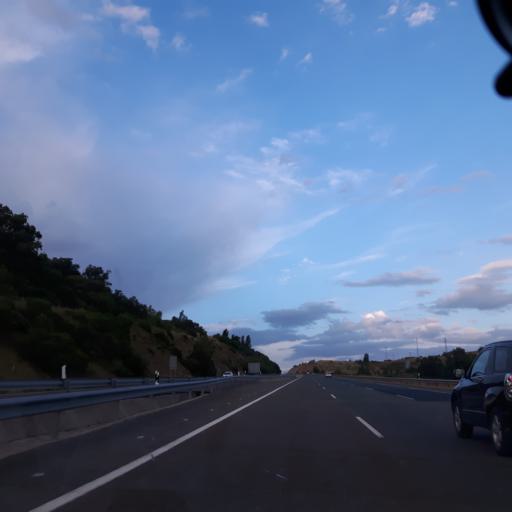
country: ES
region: Castille and Leon
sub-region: Provincia de Salamanca
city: Fresnedoso
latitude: 40.4280
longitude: -5.6998
